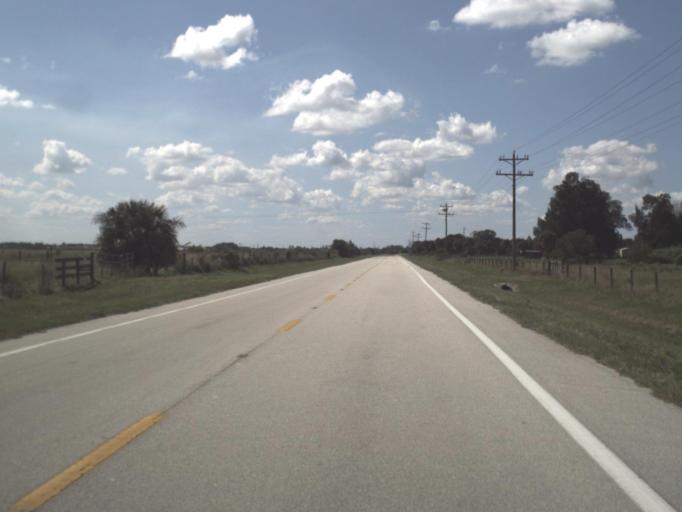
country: US
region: Florida
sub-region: Hendry County
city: Port LaBelle
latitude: 26.8124
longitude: -81.2652
